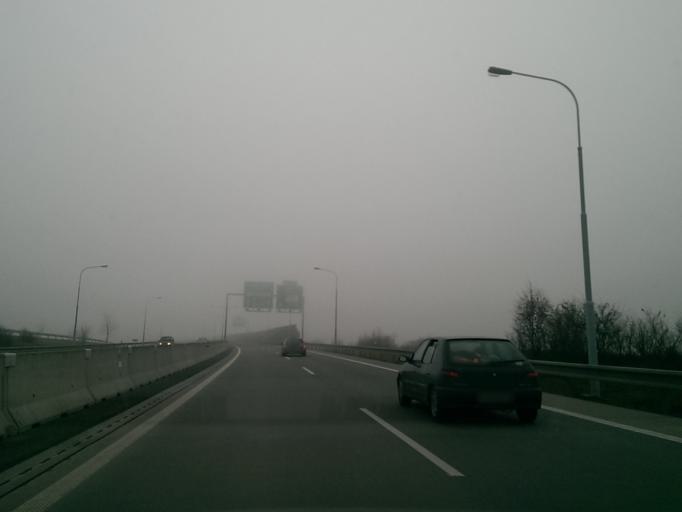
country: CZ
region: Olomoucky
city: Hnevotin
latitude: 49.5778
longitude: 17.2084
